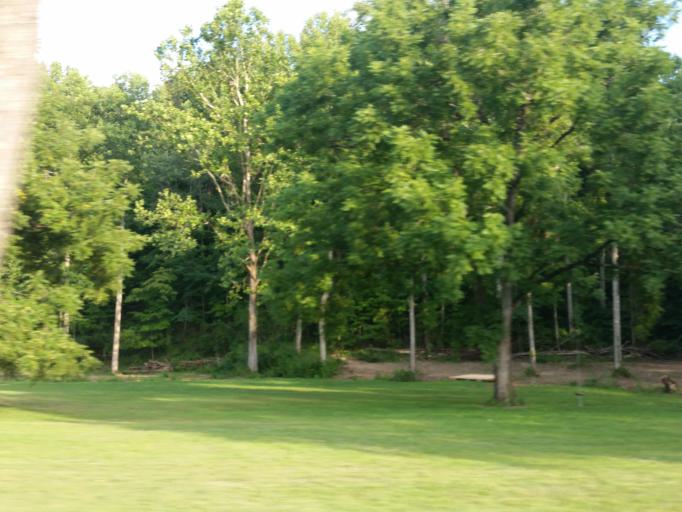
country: US
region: Tennessee
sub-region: Knox County
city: Knoxville
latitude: 36.0378
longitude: -83.9609
